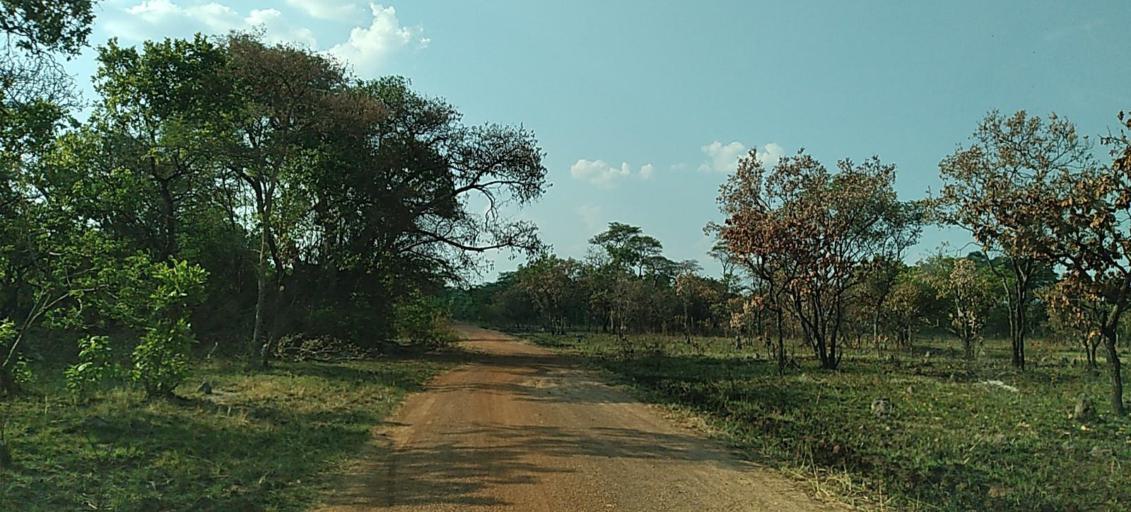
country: ZM
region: Copperbelt
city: Mpongwe
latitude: -13.4373
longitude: 28.0595
